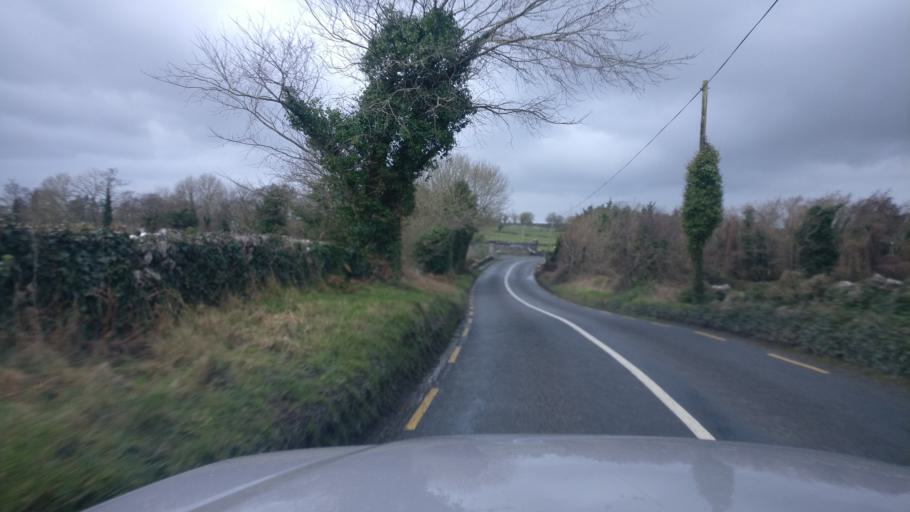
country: IE
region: Connaught
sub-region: County Galway
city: Loughrea
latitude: 53.1719
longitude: -8.6846
